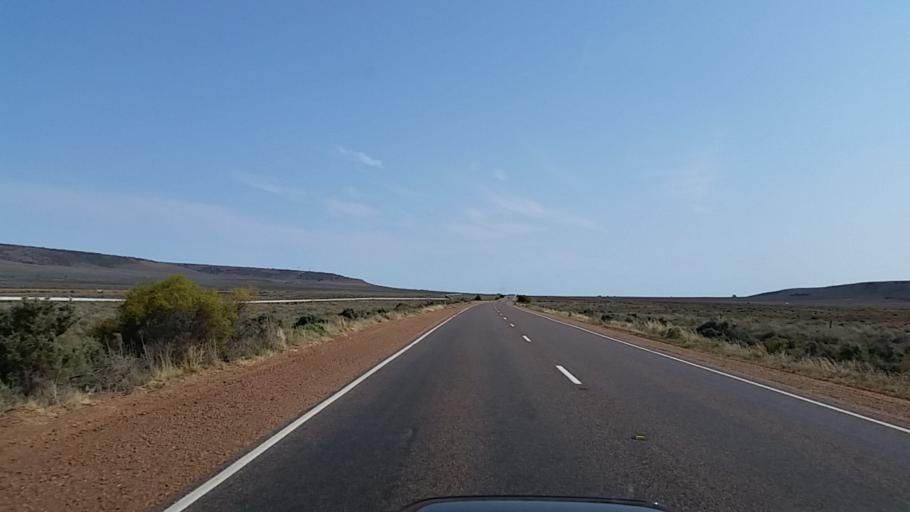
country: AU
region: South Australia
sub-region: Port Augusta
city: Port Augusta West
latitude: -32.5842
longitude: 137.6173
